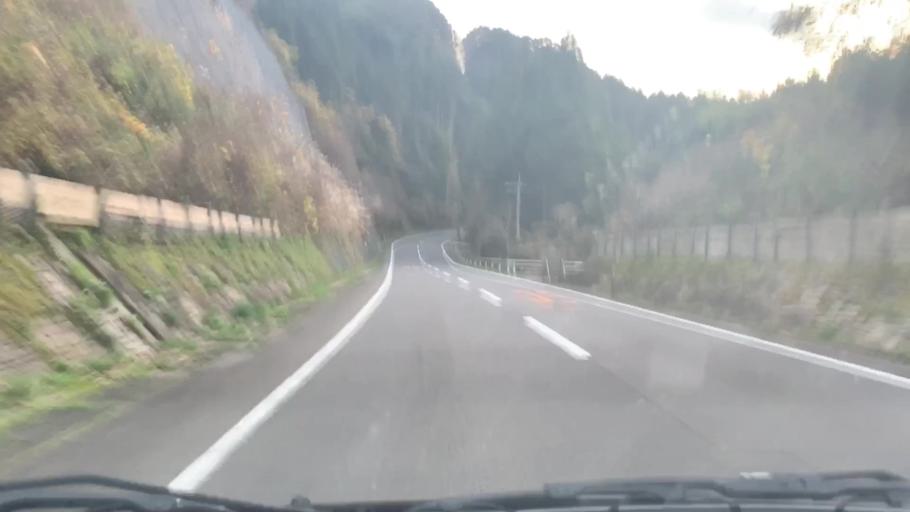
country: JP
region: Saga Prefecture
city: Kashima
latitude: 33.0178
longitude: 130.0672
